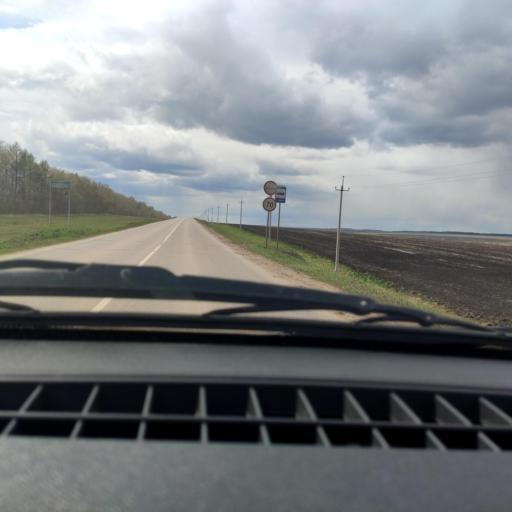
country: RU
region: Bashkortostan
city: Chekmagush
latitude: 55.1122
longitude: 54.9009
